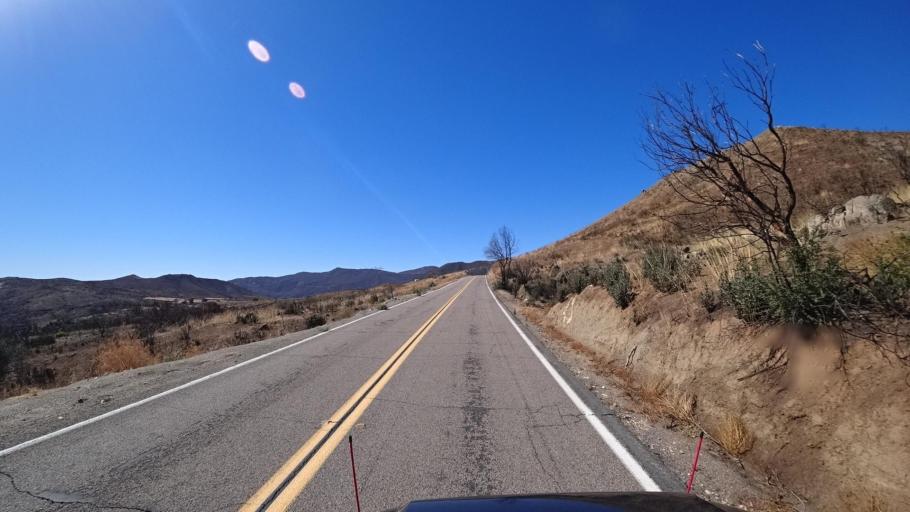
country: US
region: California
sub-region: San Diego County
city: Alpine
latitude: 32.7285
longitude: -116.6953
